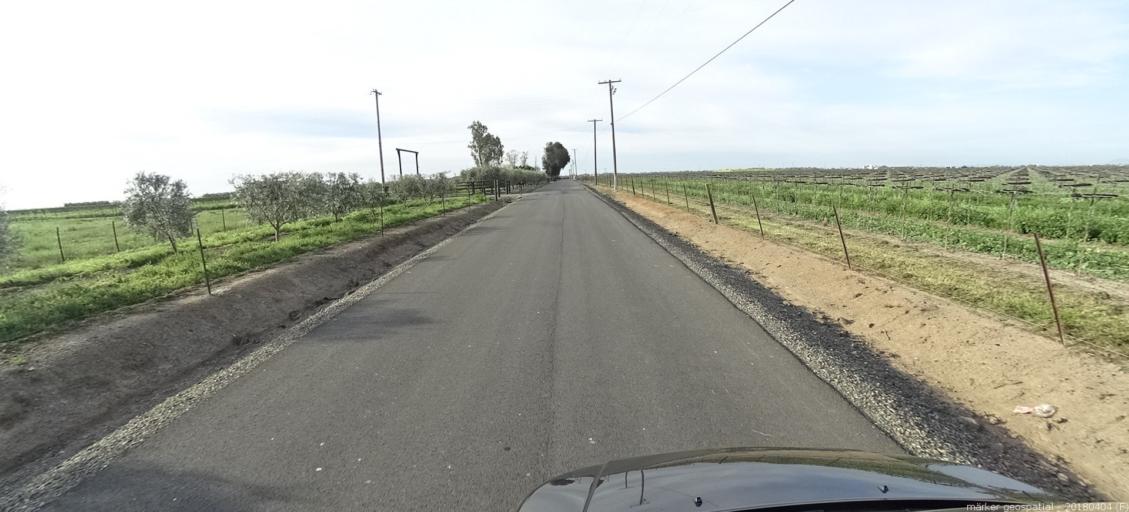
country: US
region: California
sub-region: Sacramento County
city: Herald
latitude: 38.3318
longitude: -121.2676
